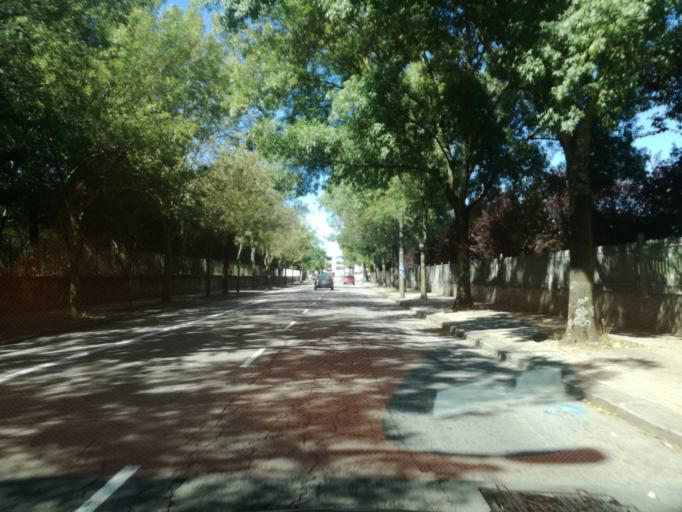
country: PT
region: Porto
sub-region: Matosinhos
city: Sao Mamede de Infesta
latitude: 41.1799
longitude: -8.5983
